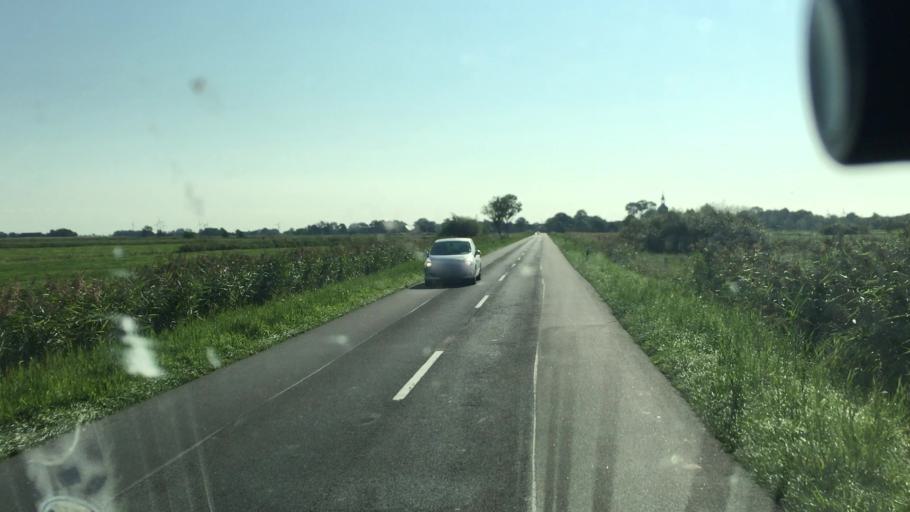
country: DE
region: Lower Saxony
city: Werdum
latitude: 53.6625
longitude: 7.7031
